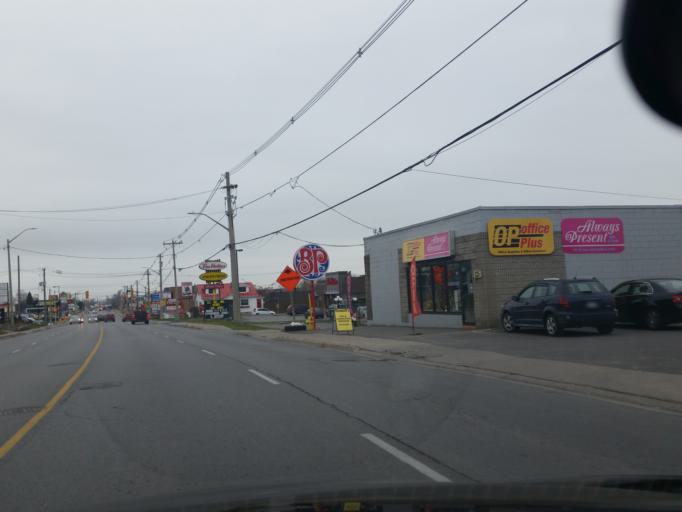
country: CA
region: Ontario
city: Quinte West
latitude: 44.1045
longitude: -77.5616
